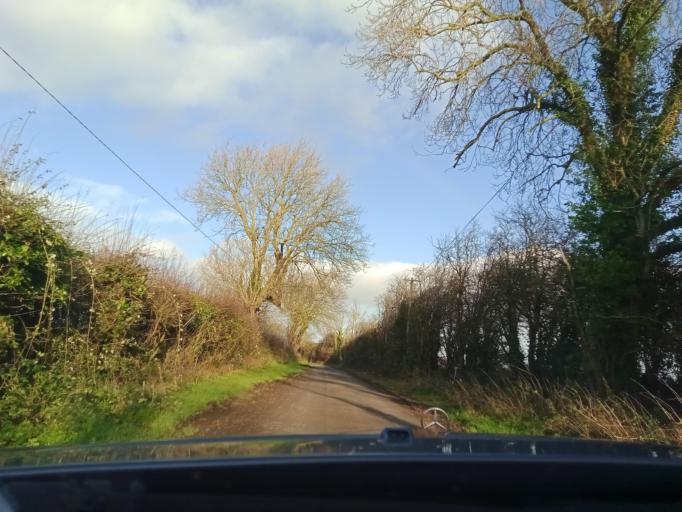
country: IE
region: Leinster
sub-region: Kilkenny
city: Callan
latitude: 52.4947
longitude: -7.3571
